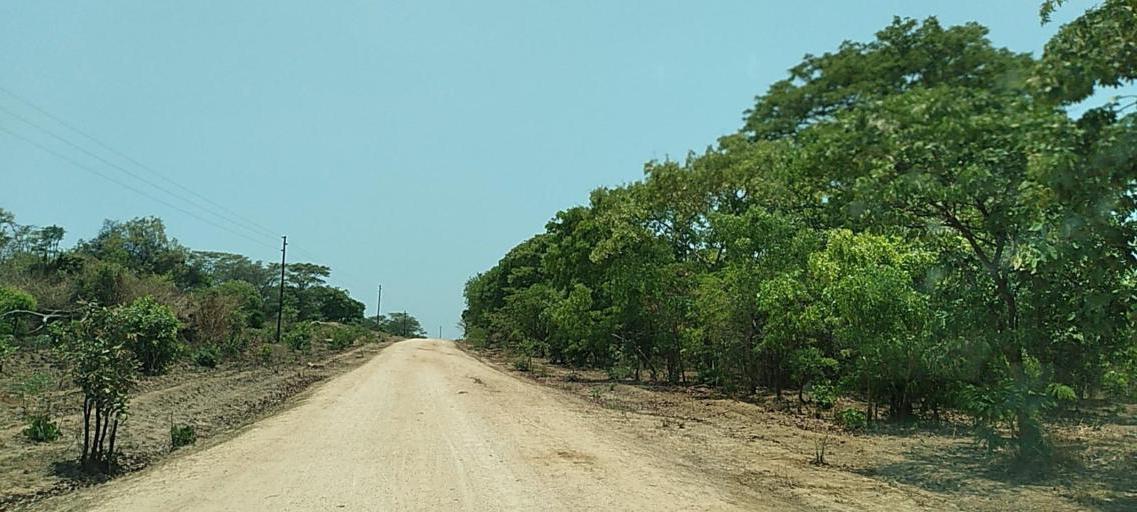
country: ZM
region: Copperbelt
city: Mpongwe
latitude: -13.8128
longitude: 27.8498
